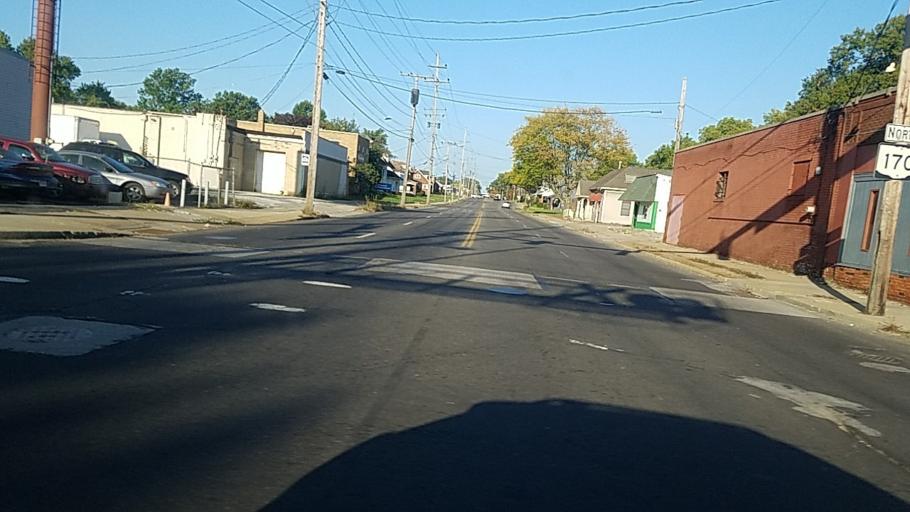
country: US
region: Ohio
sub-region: Mahoning County
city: Boardman
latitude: 41.0608
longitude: -80.6579
